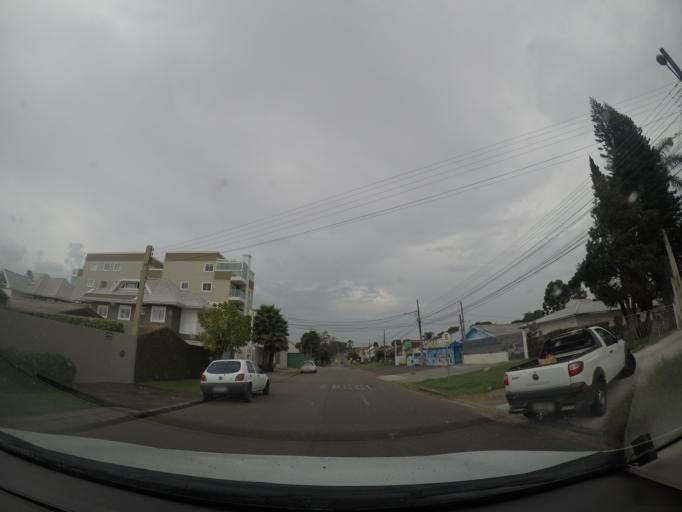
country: BR
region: Parana
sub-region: Sao Jose Dos Pinhais
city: Sao Jose dos Pinhais
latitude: -25.5088
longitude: -49.2489
